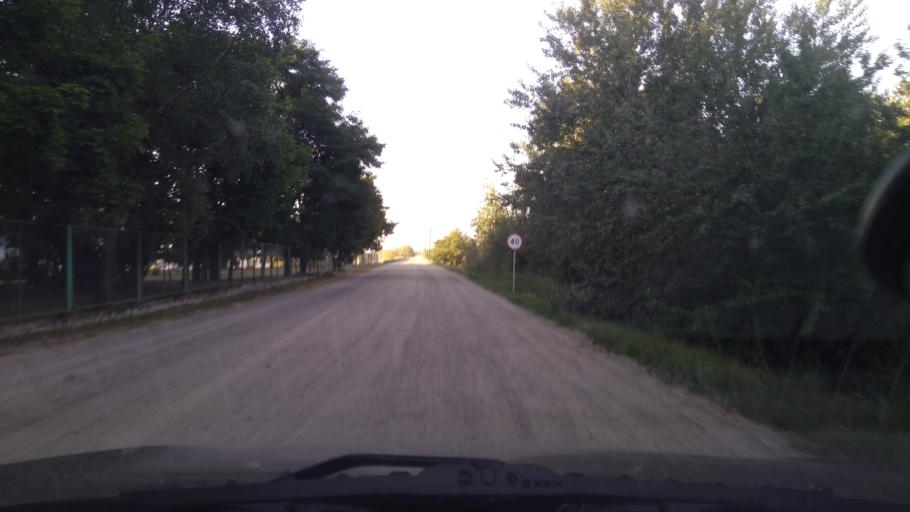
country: BY
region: Brest
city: Byaroza
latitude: 52.6016
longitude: 24.8774
